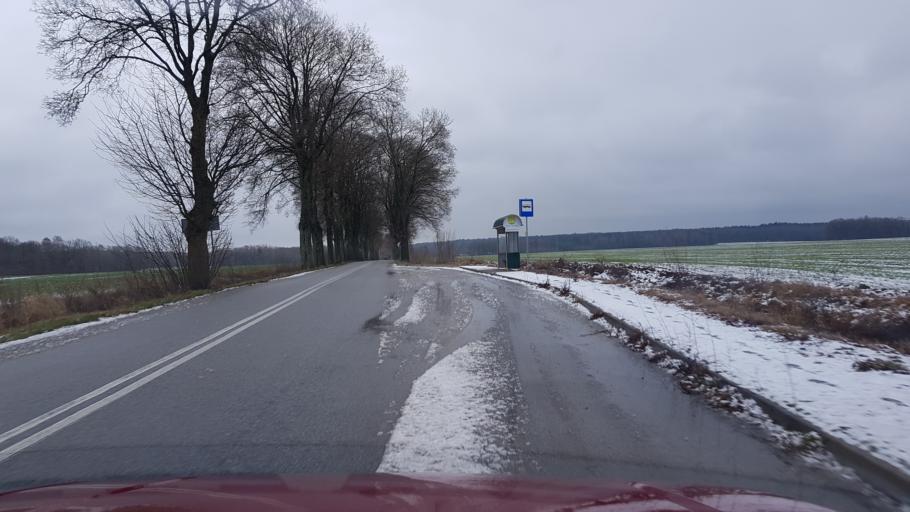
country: PL
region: West Pomeranian Voivodeship
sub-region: Powiat lobeski
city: Resko
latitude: 53.8292
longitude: 15.3893
